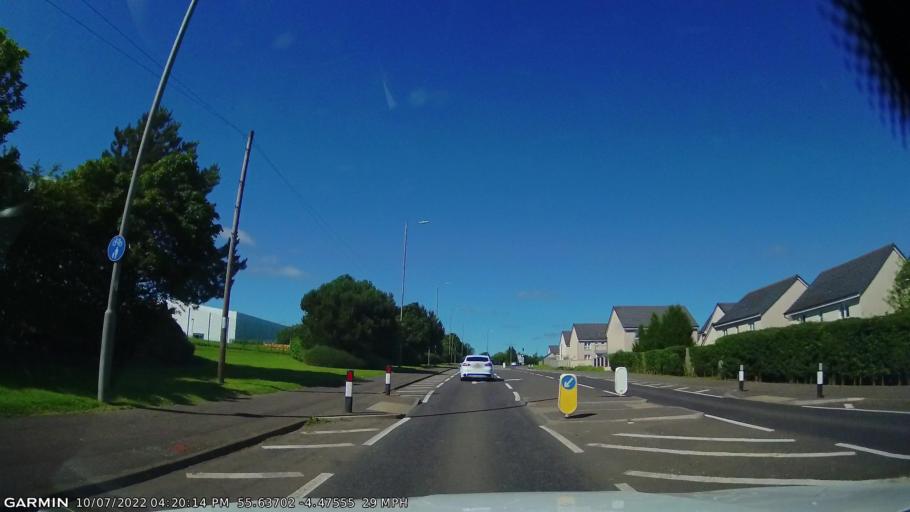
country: GB
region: Scotland
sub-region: East Ayrshire
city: Kilmarnock
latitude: 55.6374
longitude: -4.4760
